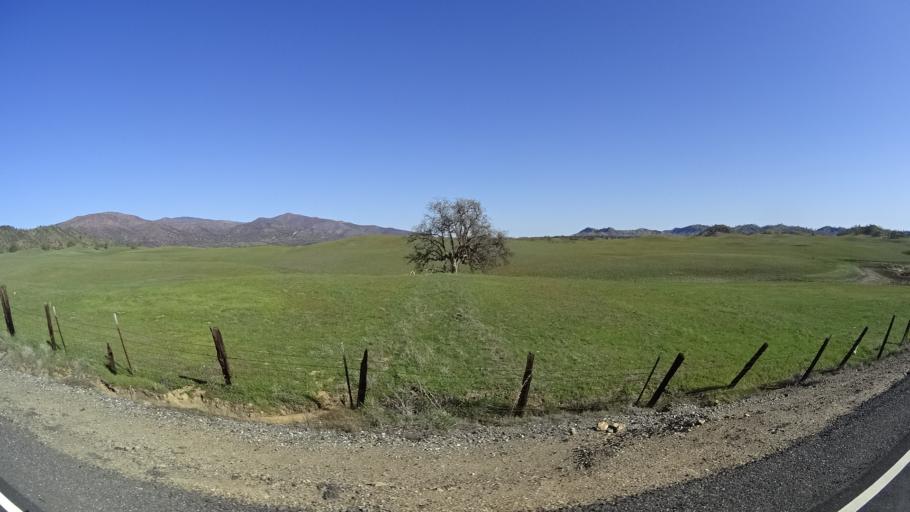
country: US
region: California
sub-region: Glenn County
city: Orland
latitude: 39.6578
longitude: -122.5533
